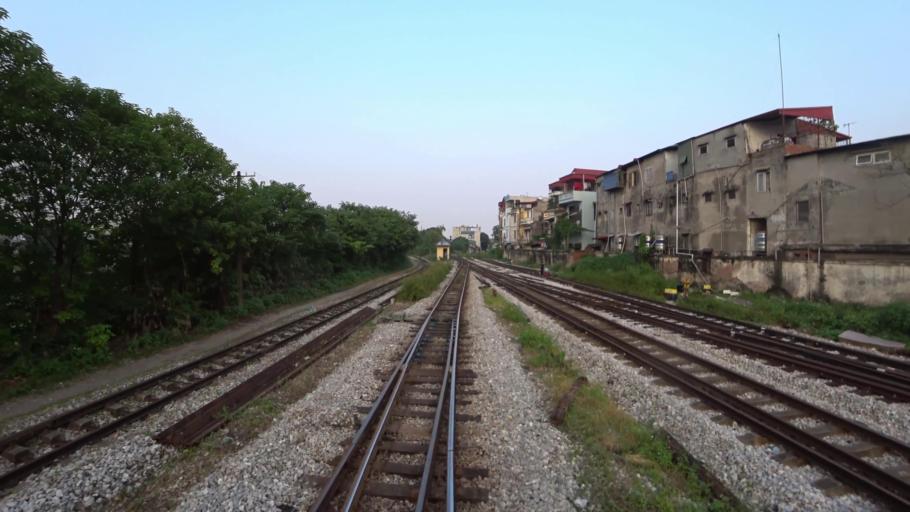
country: VN
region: Ha Noi
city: Trau Quy
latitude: 21.0679
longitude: 105.8991
